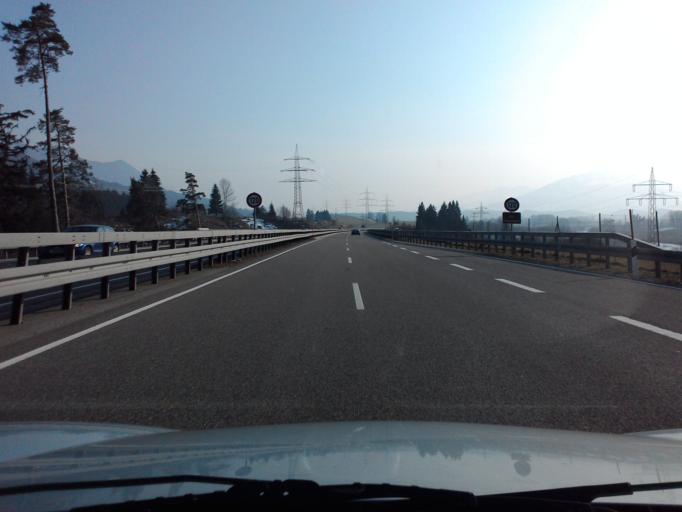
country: DE
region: Bavaria
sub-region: Swabia
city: Rettenberg
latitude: 47.6082
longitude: 10.2736
